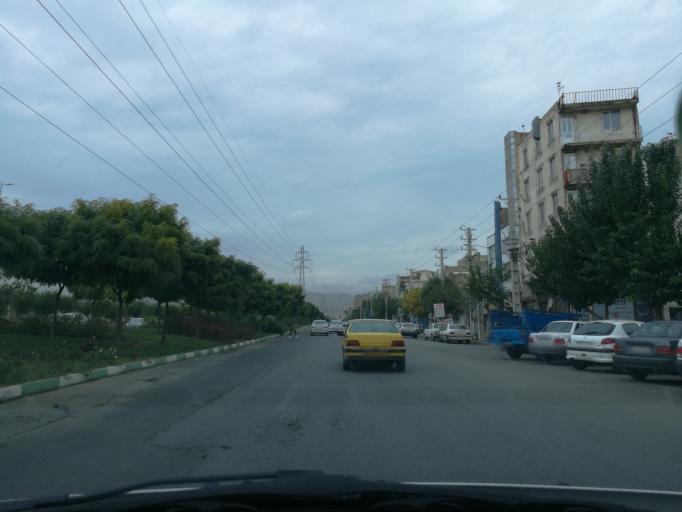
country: IR
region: Alborz
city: Karaj
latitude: 35.8503
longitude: 50.9176
